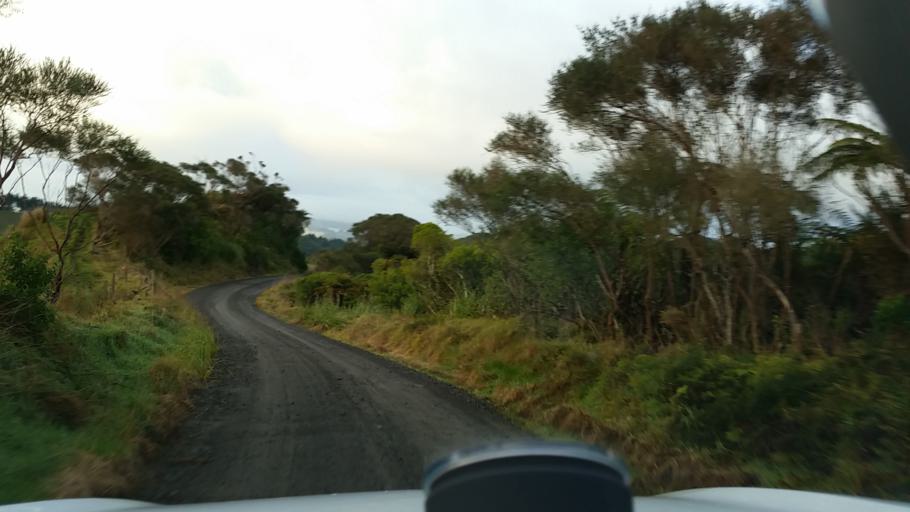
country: NZ
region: Taranaki
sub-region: South Taranaki District
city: Eltham
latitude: -39.4408
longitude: 174.4502
